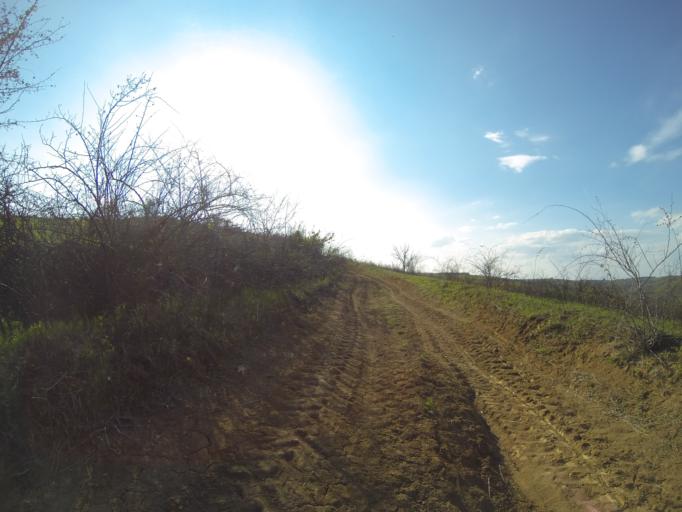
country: RO
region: Gorj
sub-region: Comuna Crusetu
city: Crusetu
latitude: 44.6008
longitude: 23.6283
